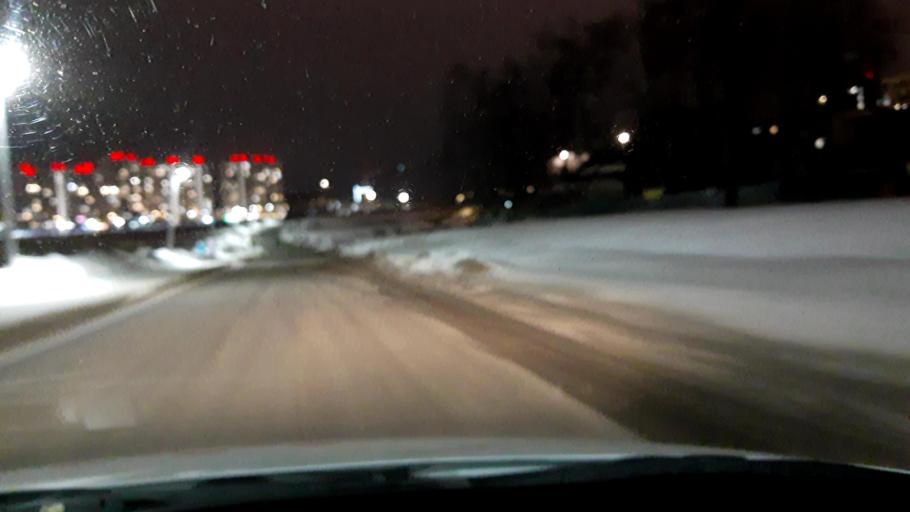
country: RU
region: Moskovskaya
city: Kommunarka
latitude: 55.5535
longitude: 37.5182
